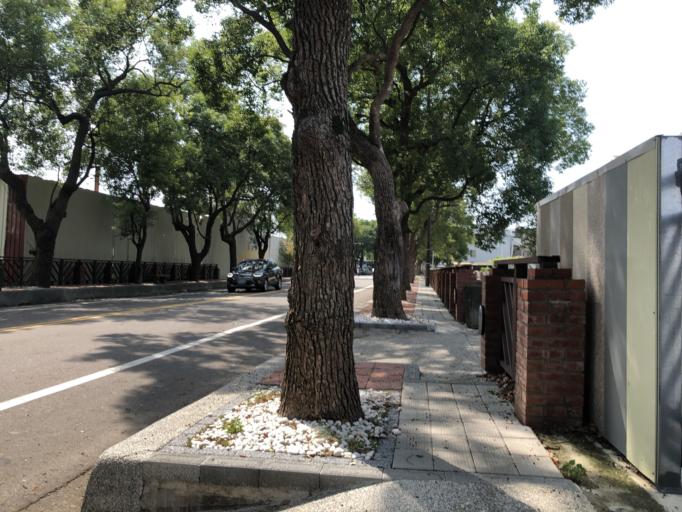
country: TW
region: Taiwan
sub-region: Miaoli
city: Miaoli
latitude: 24.4822
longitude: 120.7886
